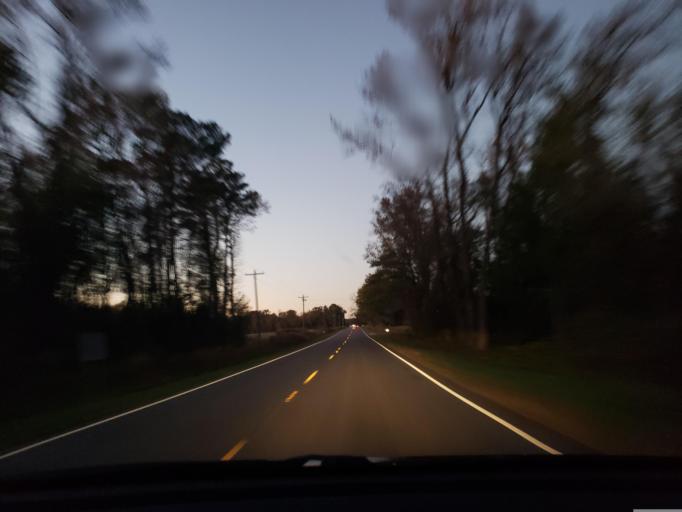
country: US
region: North Carolina
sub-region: Duplin County
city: Kenansville
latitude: 34.9304
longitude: -77.9398
